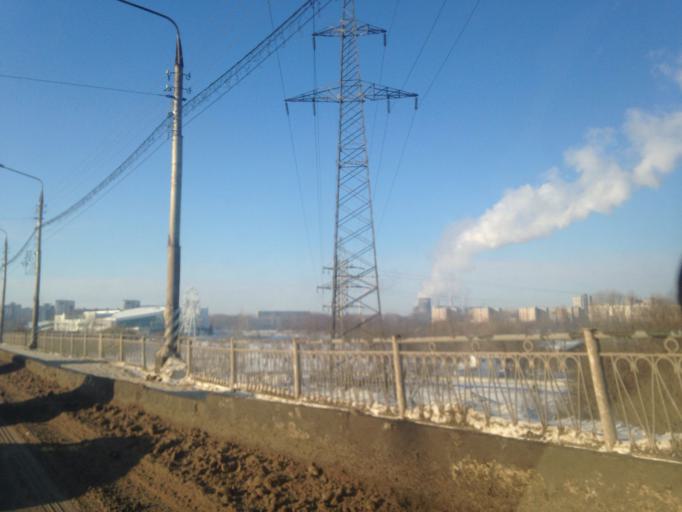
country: RU
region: Ulyanovsk
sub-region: Ulyanovskiy Rayon
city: Ulyanovsk
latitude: 54.3064
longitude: 48.3704
